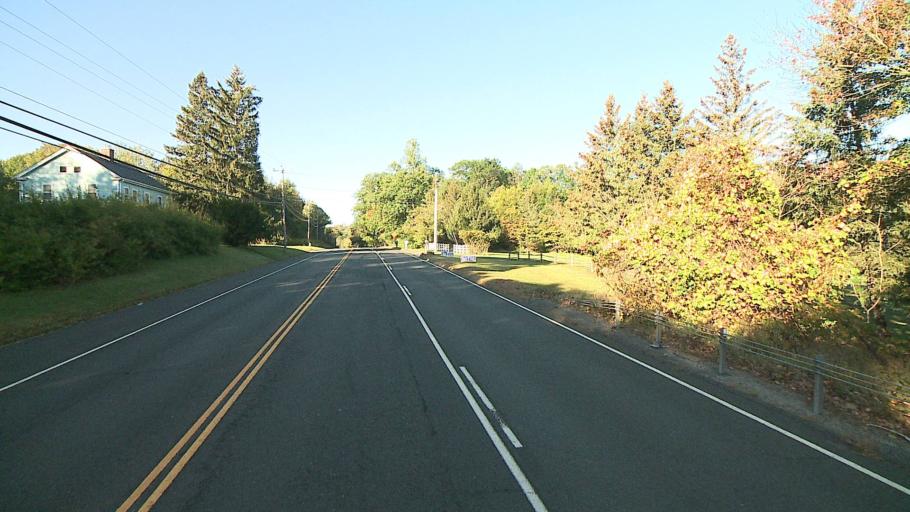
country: US
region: Connecticut
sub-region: Litchfield County
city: Northwest Harwinton
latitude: 41.8280
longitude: -73.0414
